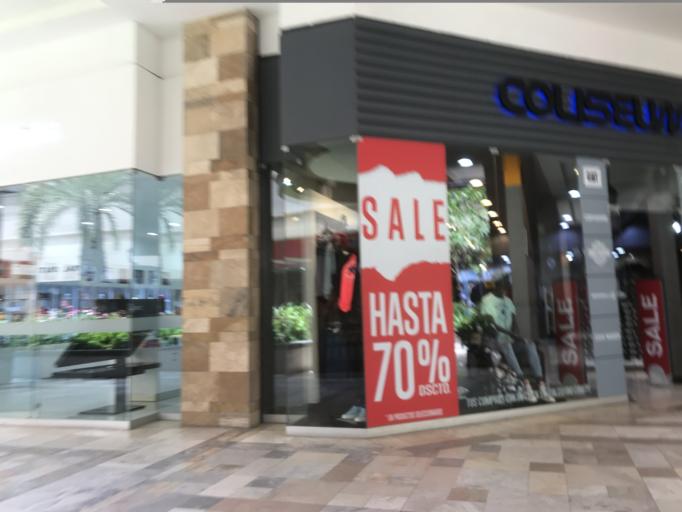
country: PE
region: Arequipa
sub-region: Provincia de Arequipa
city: Arequipa
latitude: -16.3745
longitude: -71.5573
